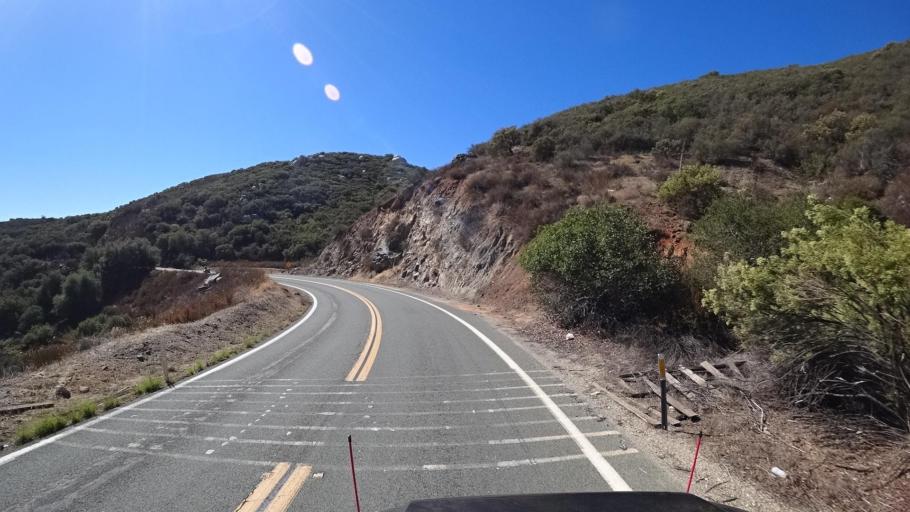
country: US
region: California
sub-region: San Diego County
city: Descanso
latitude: 32.7514
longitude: -116.6700
